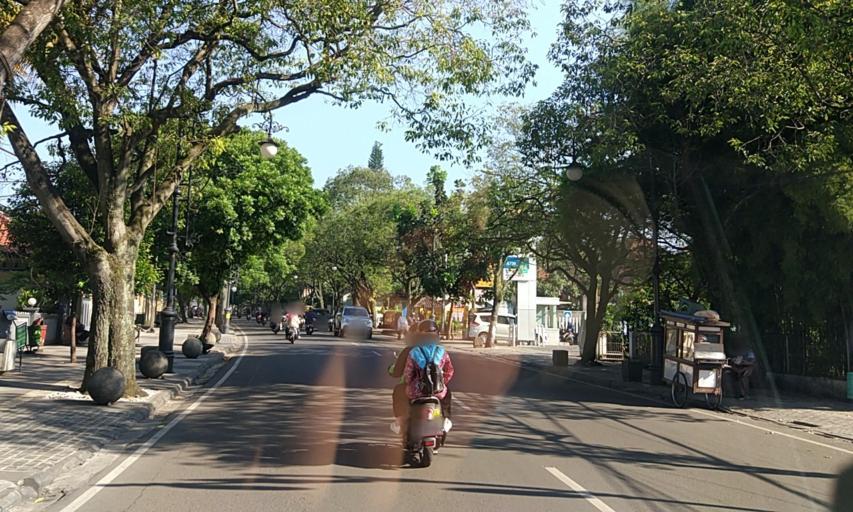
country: ID
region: West Java
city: Bandung
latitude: -6.9069
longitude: 107.6227
